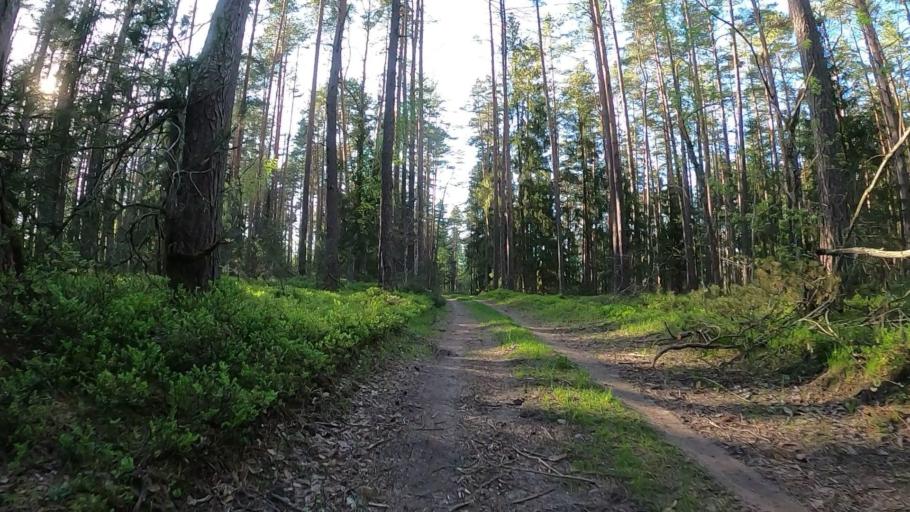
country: LV
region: Baldone
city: Baldone
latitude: 56.7710
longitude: 24.3435
